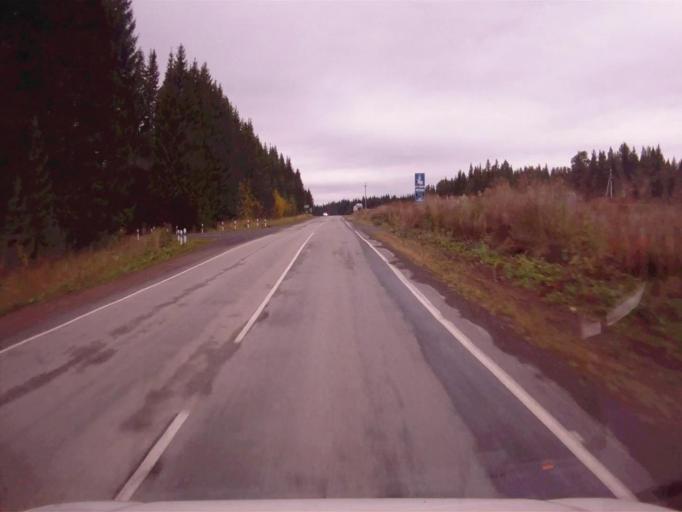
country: RU
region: Chelyabinsk
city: Nyazepetrovsk
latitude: 56.0660
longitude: 59.6516
